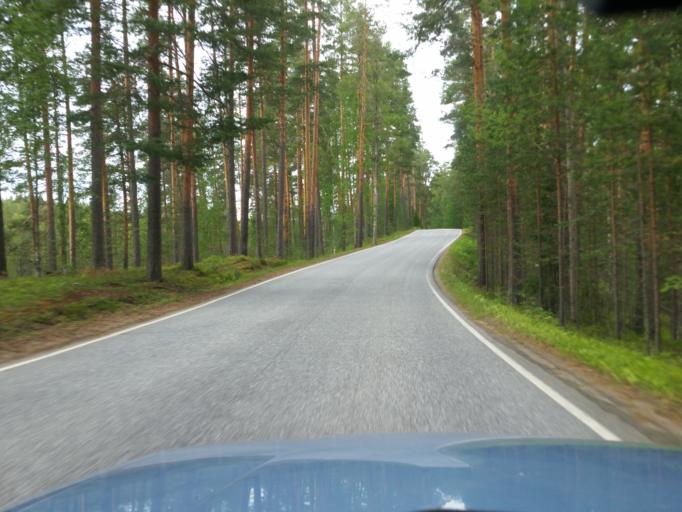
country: FI
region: Southern Savonia
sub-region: Savonlinna
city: Sulkava
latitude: 61.7824
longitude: 28.4252
